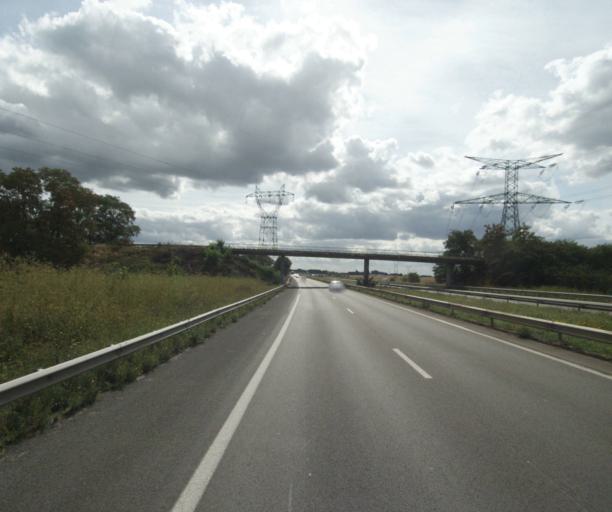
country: FR
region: Nord-Pas-de-Calais
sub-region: Departement du Nord
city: Orchies
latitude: 50.4896
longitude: 3.2136
